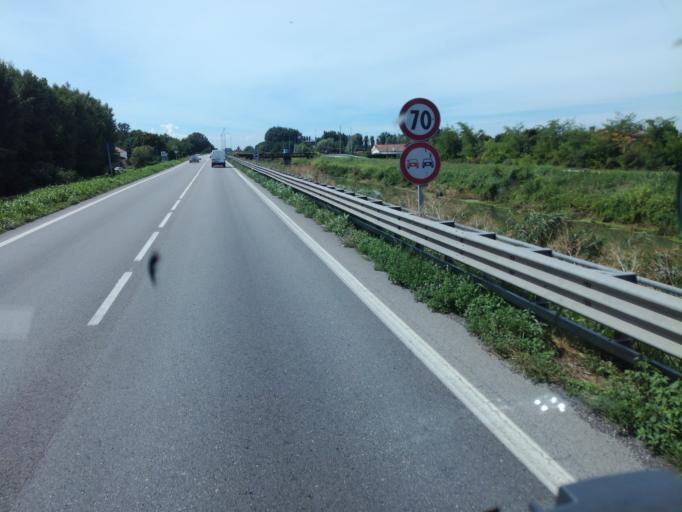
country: IT
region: Veneto
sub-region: Provincia di Venezia
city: Campagna Lupia
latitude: 45.3690
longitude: 12.1380
